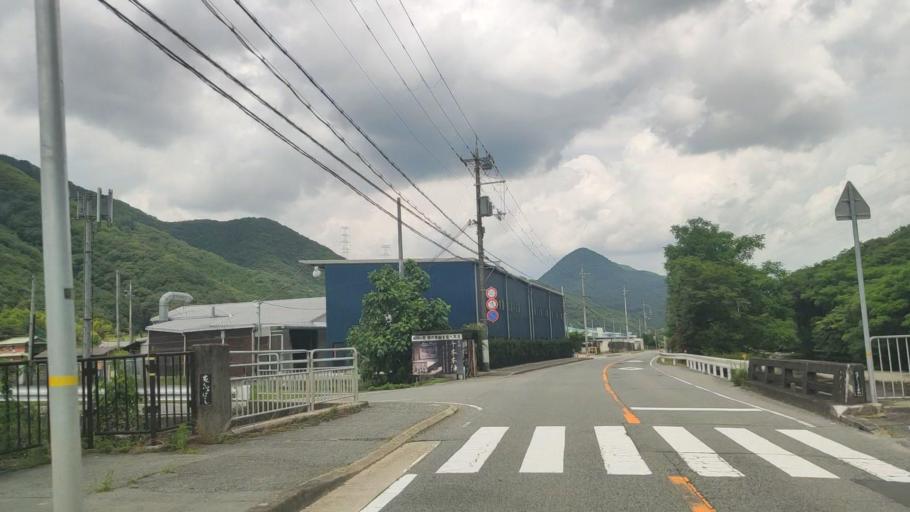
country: JP
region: Hyogo
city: Yamazakicho-nakabirose
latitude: 34.9410
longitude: 134.4892
